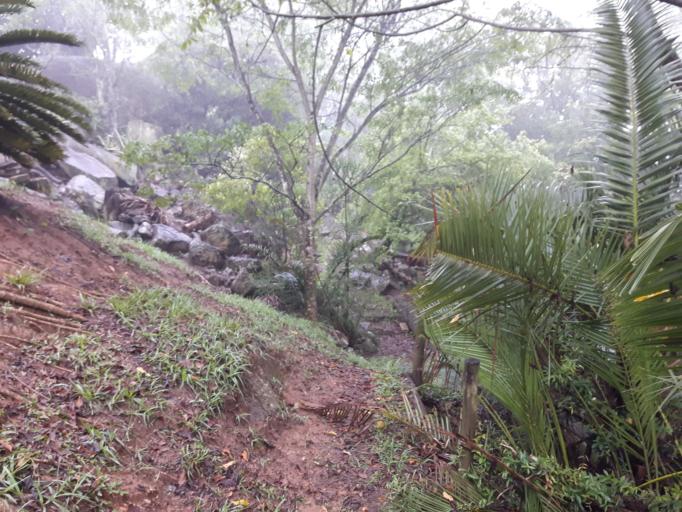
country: SZ
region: Hhohho
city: Lobamba
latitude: -26.4704
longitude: 31.1800
